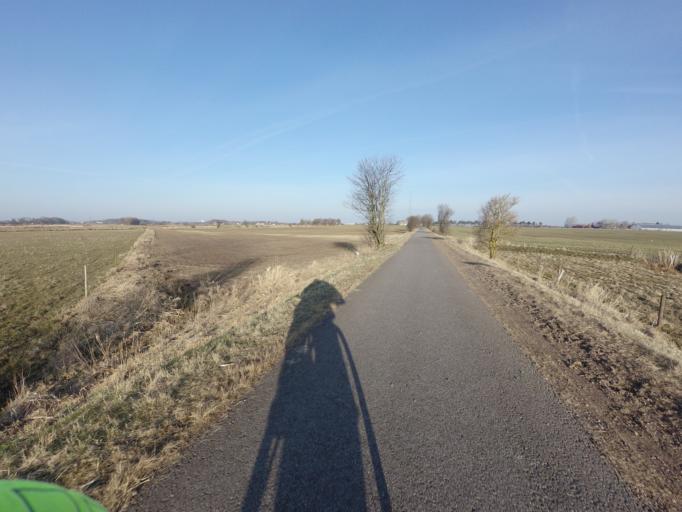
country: SE
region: Skane
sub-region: Hoganas Kommun
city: Hoganas
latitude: 56.1907
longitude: 12.6182
